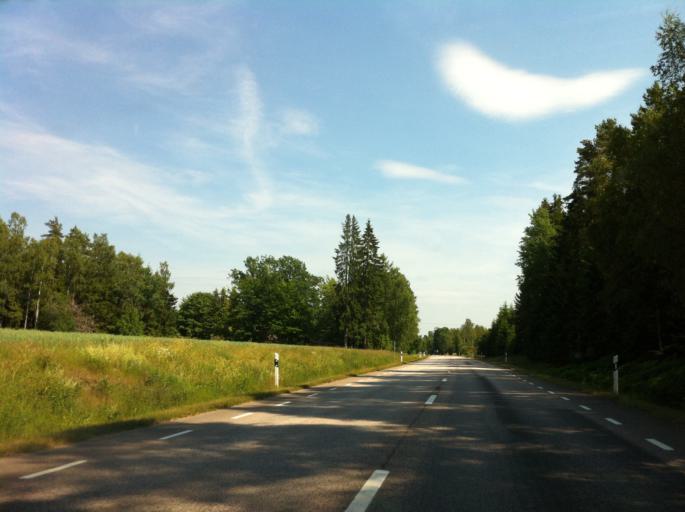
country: SE
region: Kalmar
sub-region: Nybro Kommun
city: Nybro
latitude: 56.8227
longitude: 15.7616
